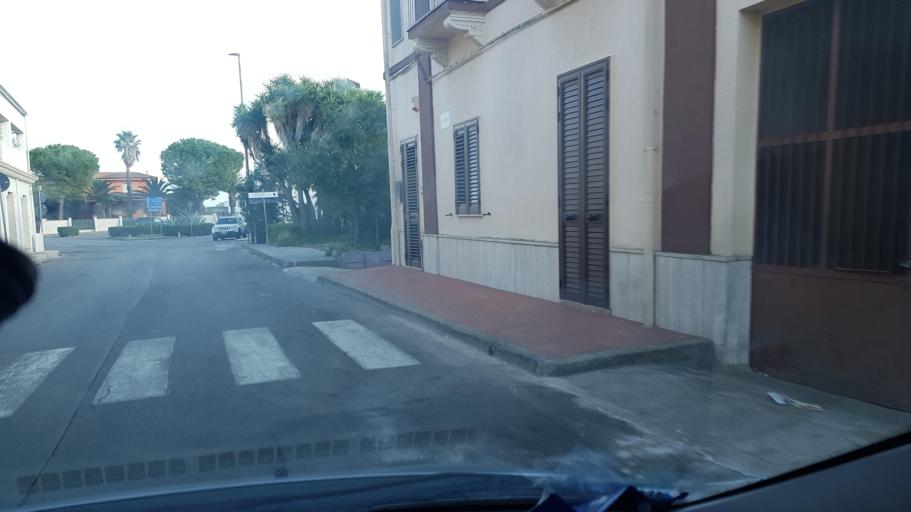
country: IT
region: Apulia
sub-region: Provincia di Lecce
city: Veglie
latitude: 40.3350
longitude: 17.9728
